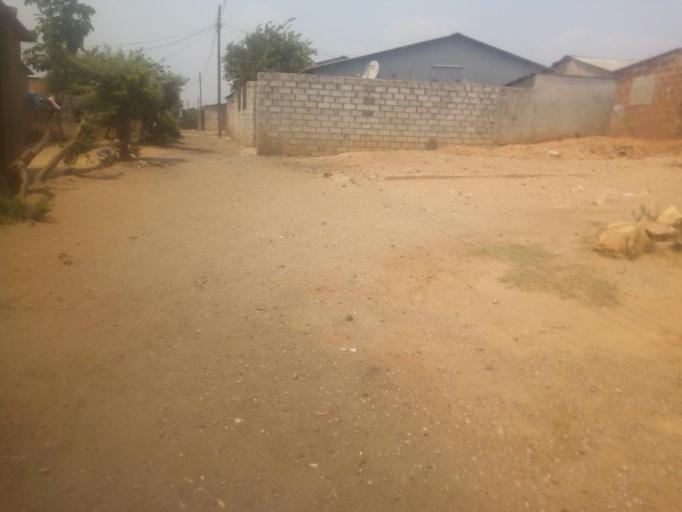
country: ZM
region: Lusaka
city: Lusaka
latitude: -15.4055
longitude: 28.3751
